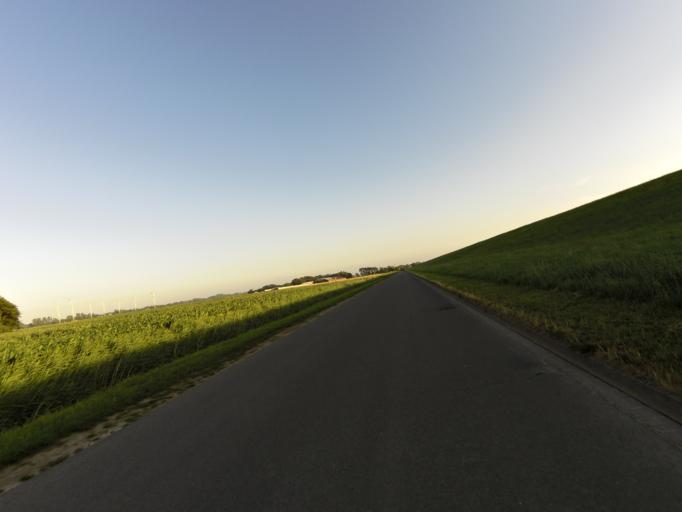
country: DE
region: Lower Saxony
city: Padingbuttel
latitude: 53.7533
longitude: 8.5314
